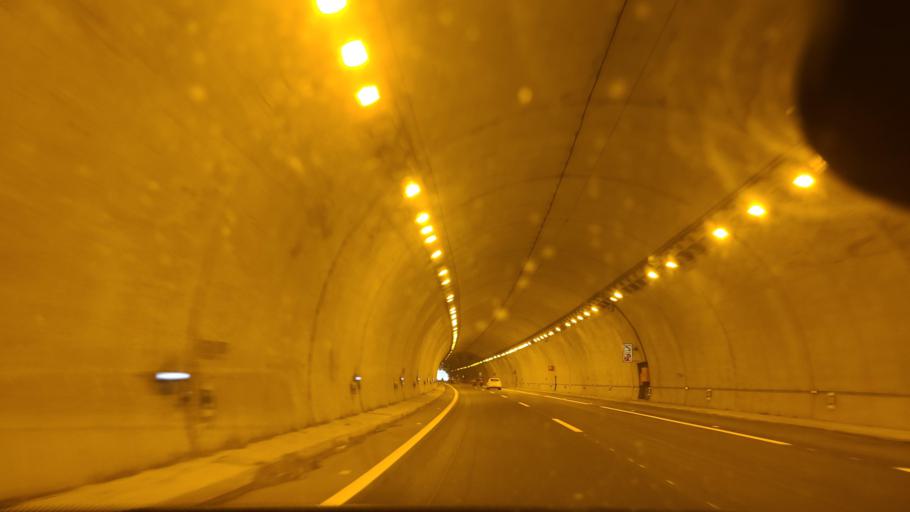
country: ES
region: Andalusia
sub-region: Provincia de Granada
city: Gualchos
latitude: 36.7197
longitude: -3.4386
